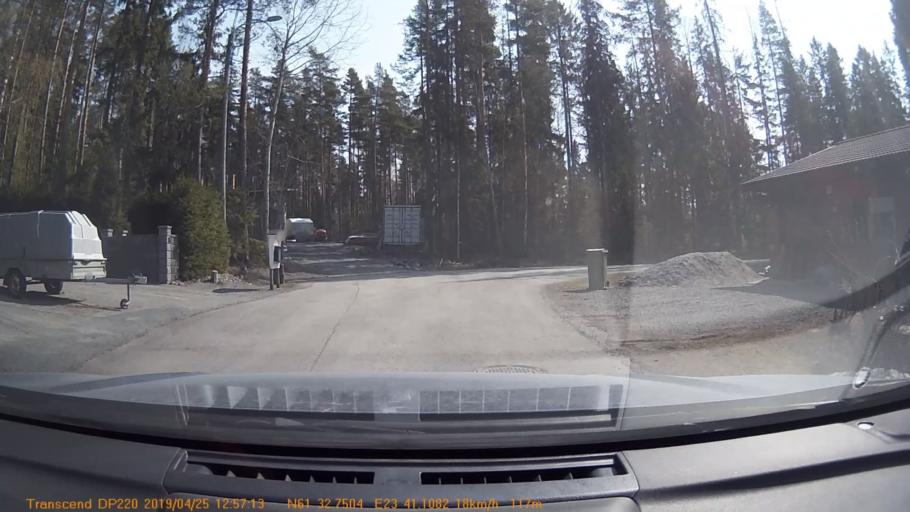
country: FI
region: Pirkanmaa
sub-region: Tampere
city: Yloejaervi
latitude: 61.5459
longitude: 23.6851
